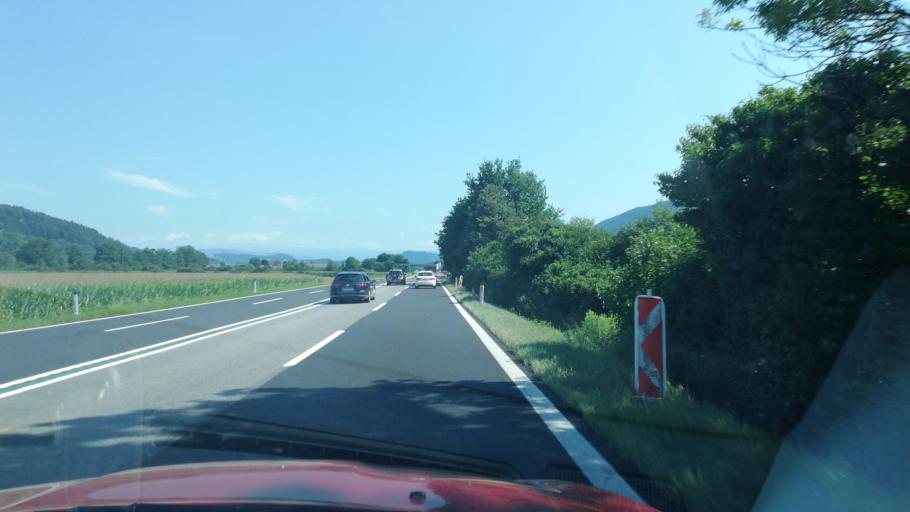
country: AT
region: Carinthia
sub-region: Politischer Bezirk Klagenfurt Land
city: Maria Saal
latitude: 46.6941
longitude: 14.3495
